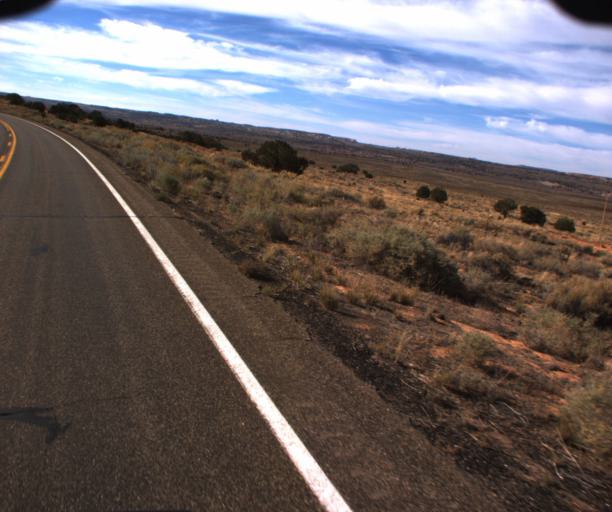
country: US
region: Arizona
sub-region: Coconino County
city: Kaibito
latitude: 36.6741
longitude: -111.2570
